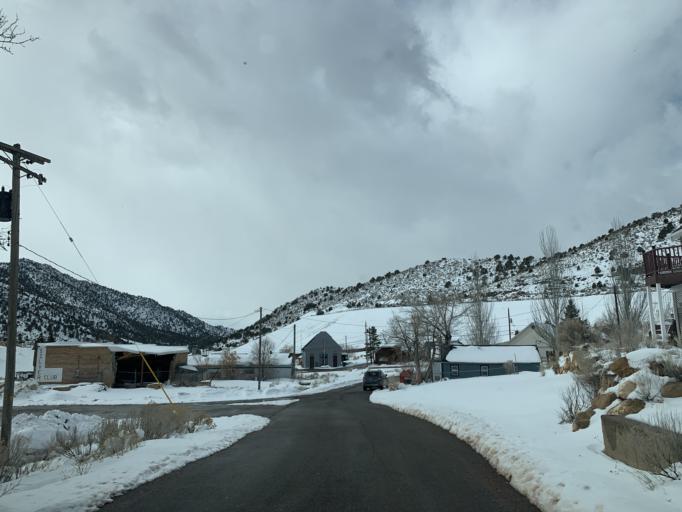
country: US
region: Utah
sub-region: Utah County
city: Genola
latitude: 39.9547
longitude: -112.1215
